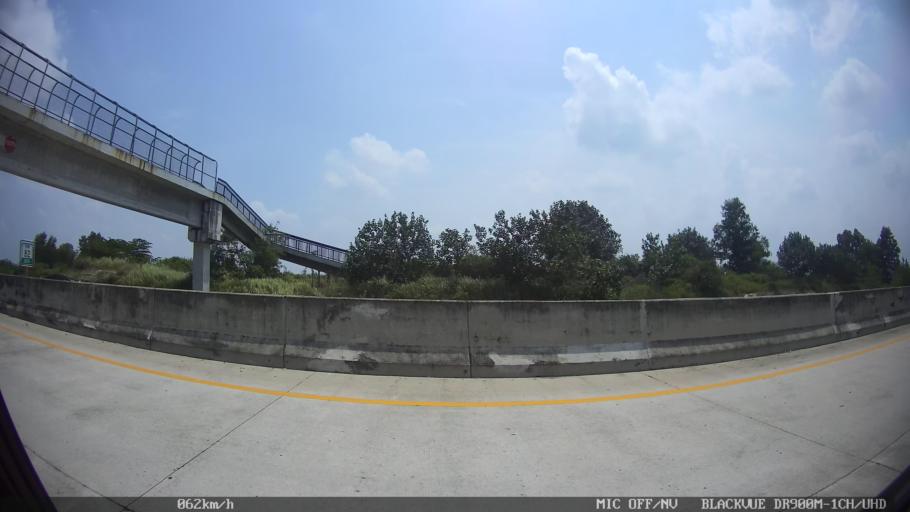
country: ID
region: Lampung
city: Kedaton
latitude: -5.3383
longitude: 105.3059
